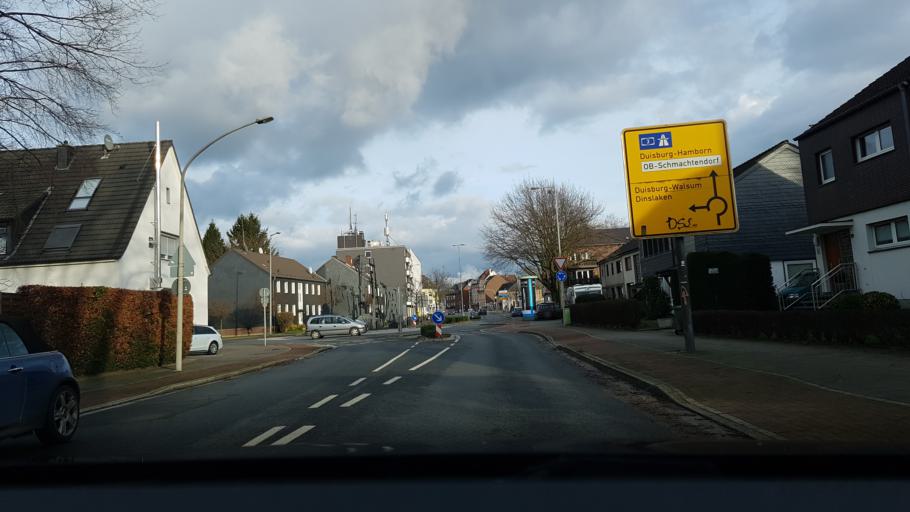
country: DE
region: North Rhine-Westphalia
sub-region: Regierungsbezirk Dusseldorf
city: Dinslaken
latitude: 51.5238
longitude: 6.7849
